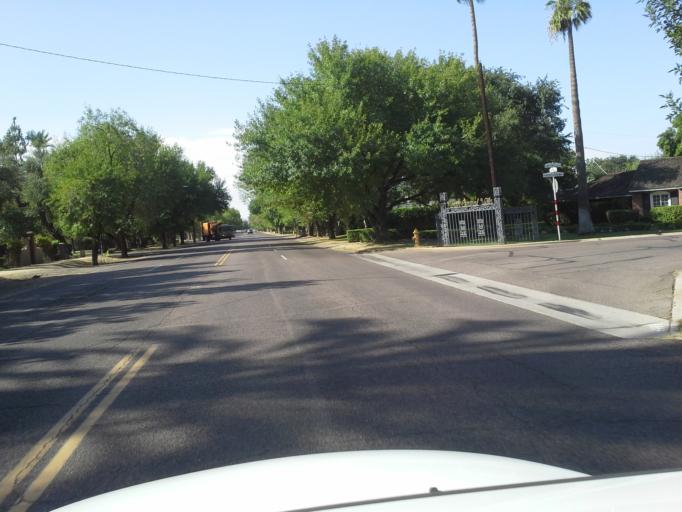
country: US
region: Arizona
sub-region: Maricopa County
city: Phoenix
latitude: 33.5427
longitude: -112.0738
